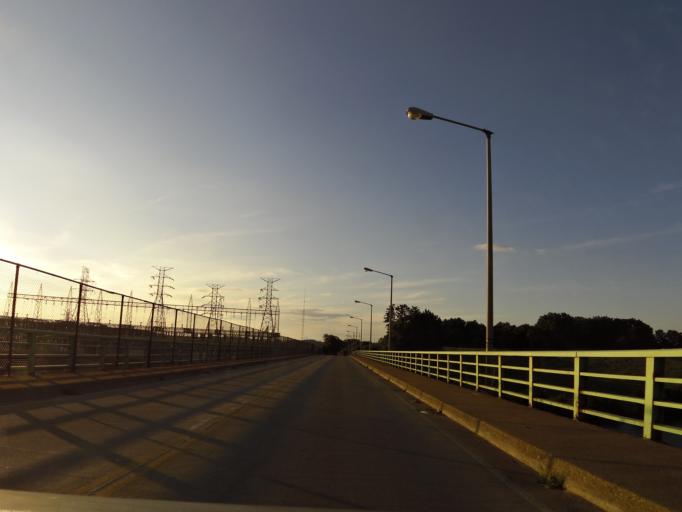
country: US
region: Tennessee
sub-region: Loudon County
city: Lenoir City
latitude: 35.7914
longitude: -84.2429
